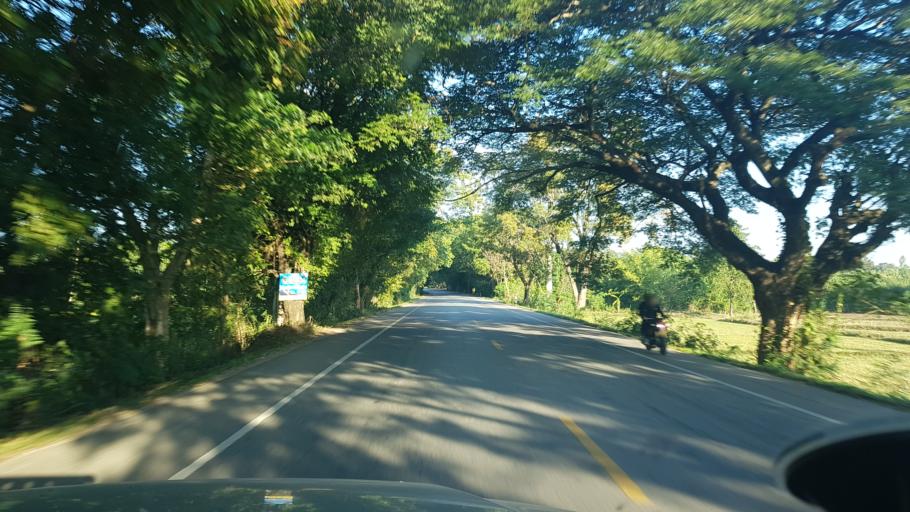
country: TH
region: Chaiyaphum
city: Khon San
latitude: 16.6118
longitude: 101.8827
